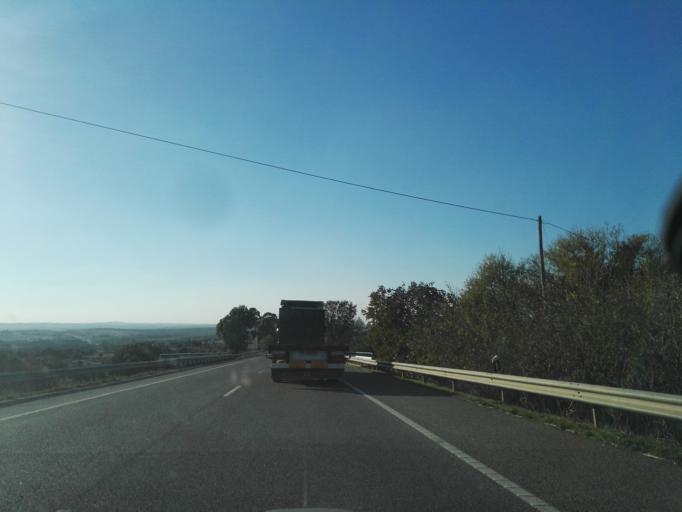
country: PT
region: Portalegre
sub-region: Elvas
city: Elvas
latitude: 38.8603
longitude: -7.2916
